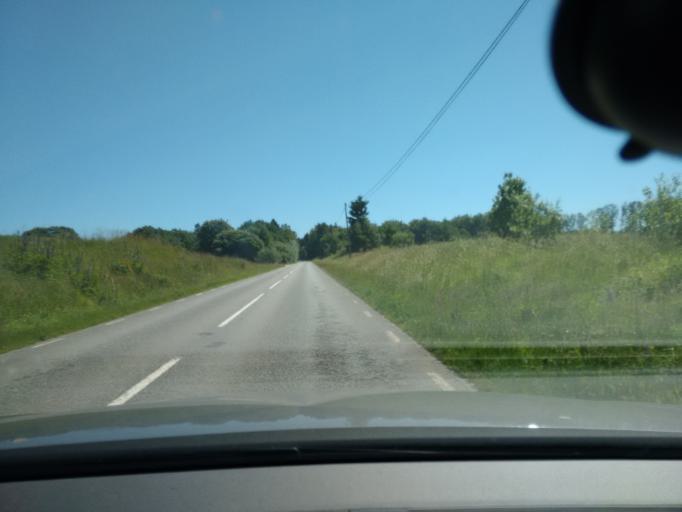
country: SE
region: Skane
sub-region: Kristianstads Kommun
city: Degeberga
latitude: 55.7600
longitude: 13.9184
